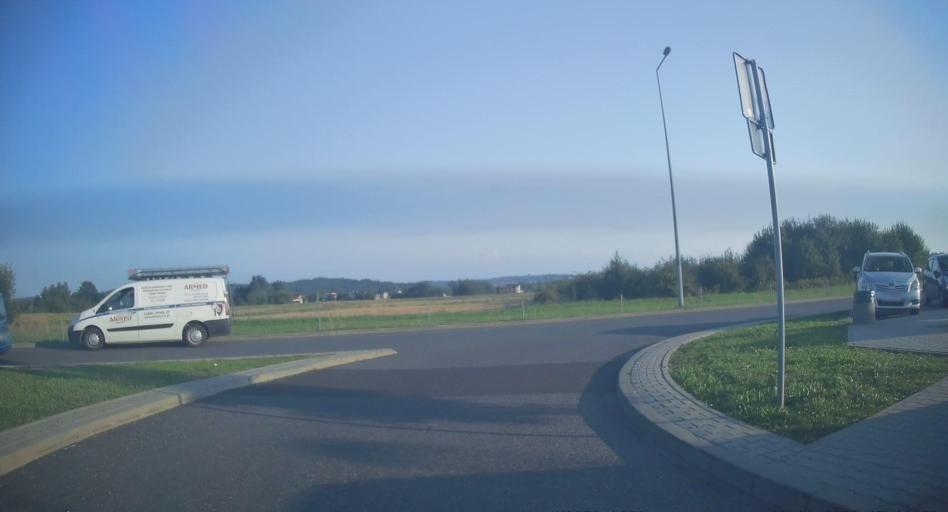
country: PL
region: Lesser Poland Voivodeship
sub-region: Powiat bochenski
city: Stanislawice
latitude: 49.9877
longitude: 20.3442
